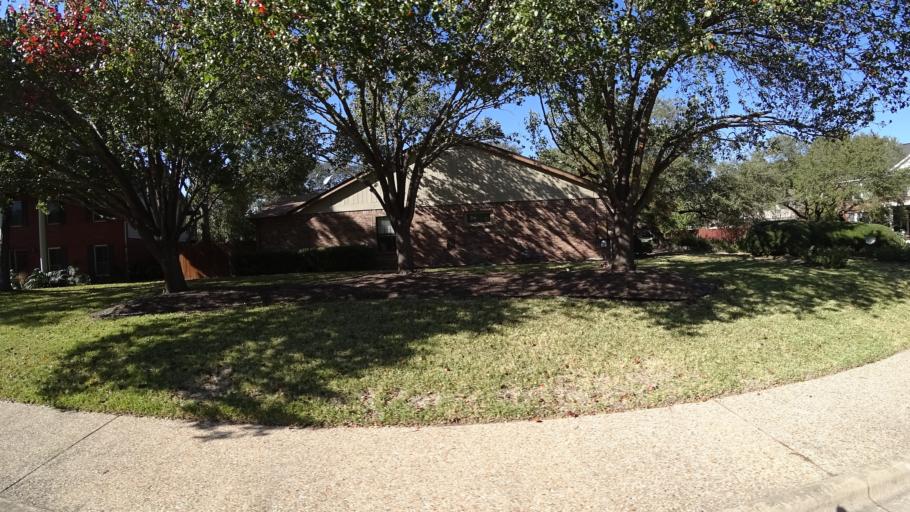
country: US
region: Texas
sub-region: Williamson County
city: Jollyville
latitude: 30.4130
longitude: -97.7685
